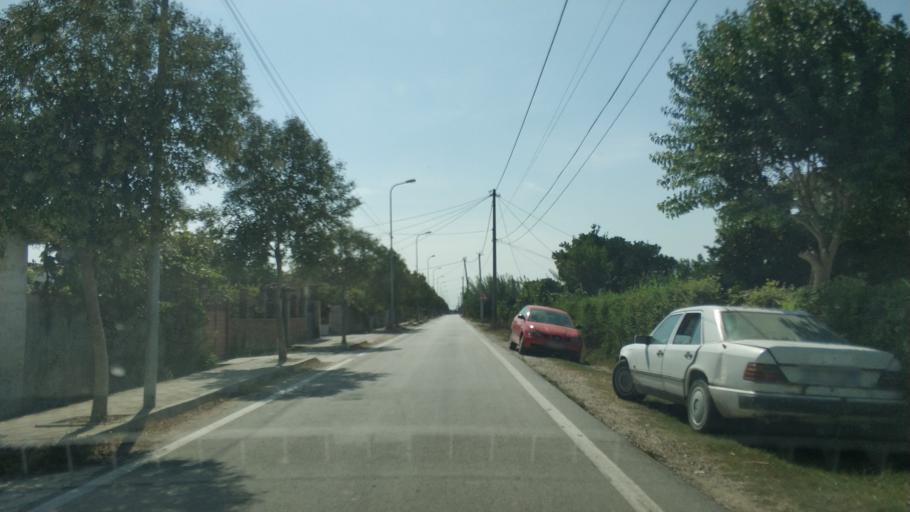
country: AL
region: Fier
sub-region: Rrethi i Fierit
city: Dermenas
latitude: 40.7346
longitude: 19.4734
